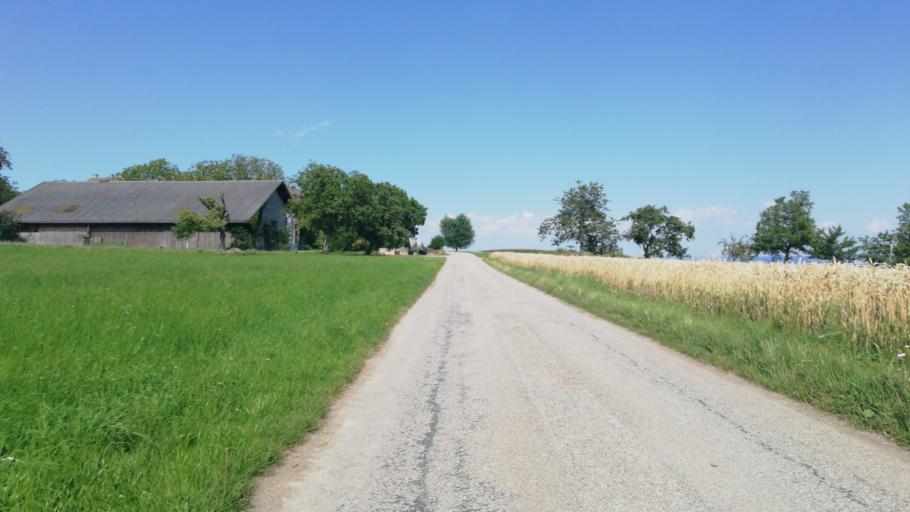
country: AT
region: Upper Austria
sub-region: Wels-Land
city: Gunskirchen
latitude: 48.1609
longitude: 13.9280
